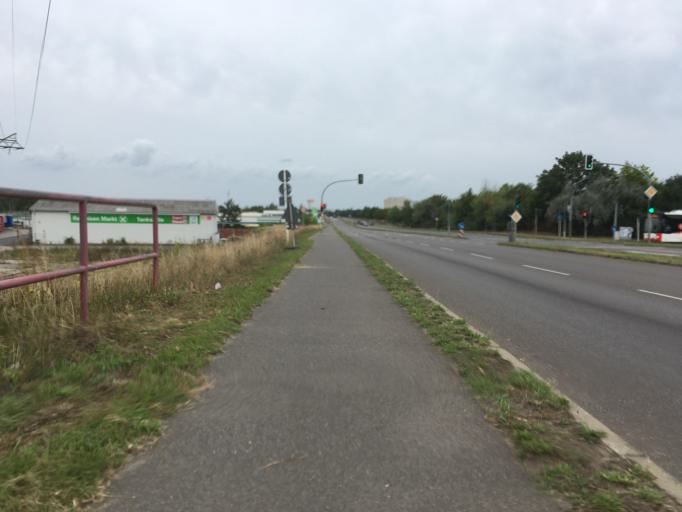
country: DE
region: Brandenburg
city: Meyenburg
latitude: 53.0745
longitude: 14.2482
